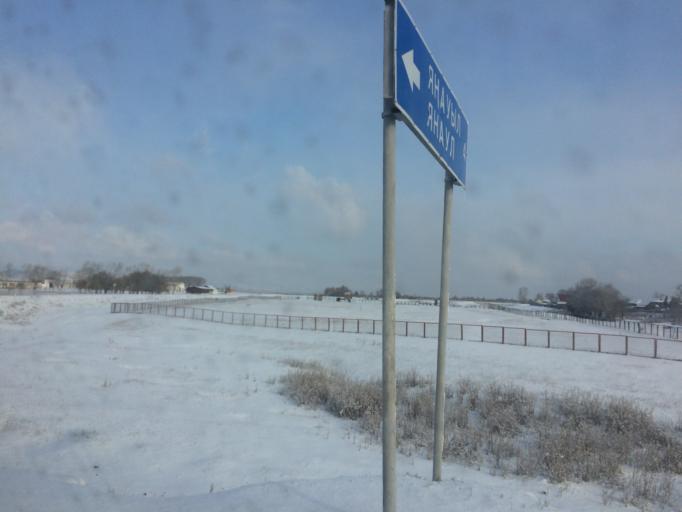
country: RU
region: Chelyabinsk
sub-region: Gorod Magnitogorsk
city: Magnitogorsk
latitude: 53.3461
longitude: 58.6647
